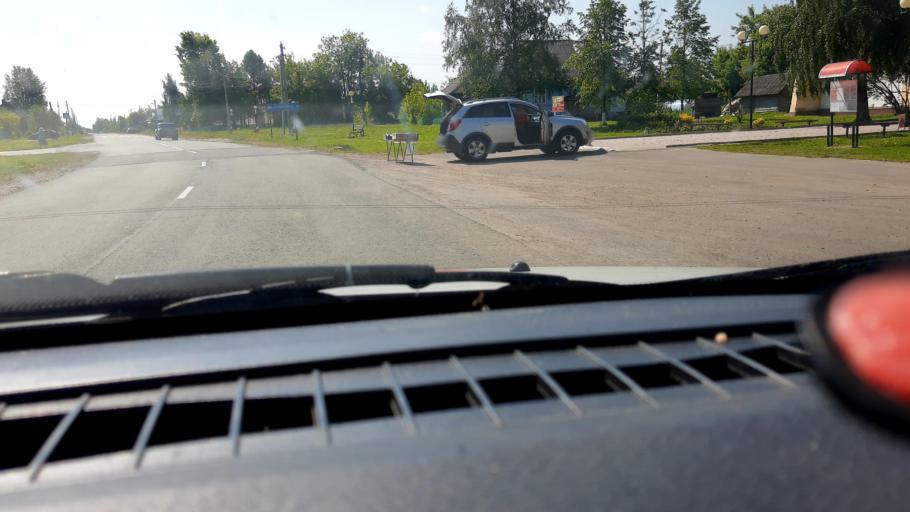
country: RU
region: Nizjnij Novgorod
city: Sharanga
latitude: 57.0508
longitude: 46.5459
